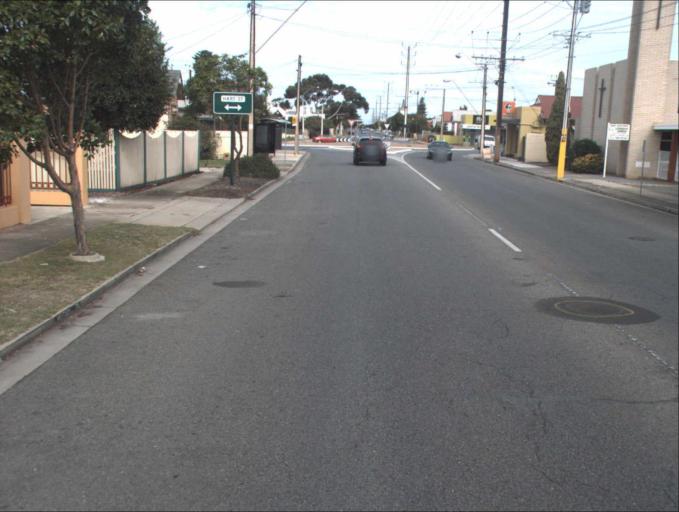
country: AU
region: South Australia
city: Port Adelaide
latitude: -34.8434
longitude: 138.4822
